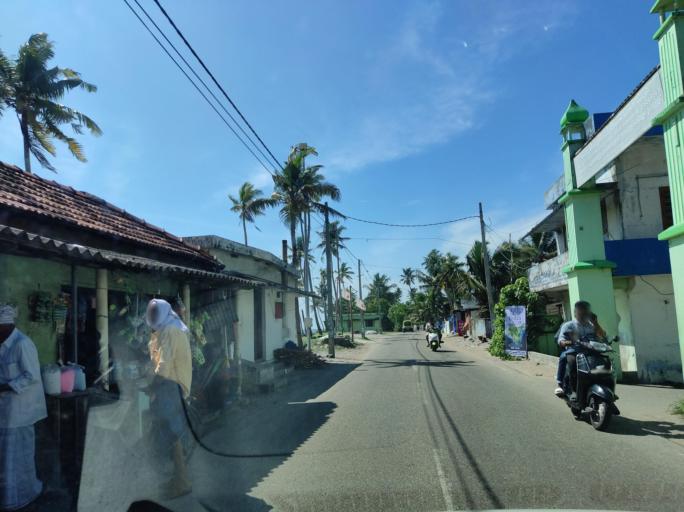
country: IN
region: Kerala
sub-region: Alappuzha
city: Kayankulam
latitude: 9.2181
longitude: 76.4262
